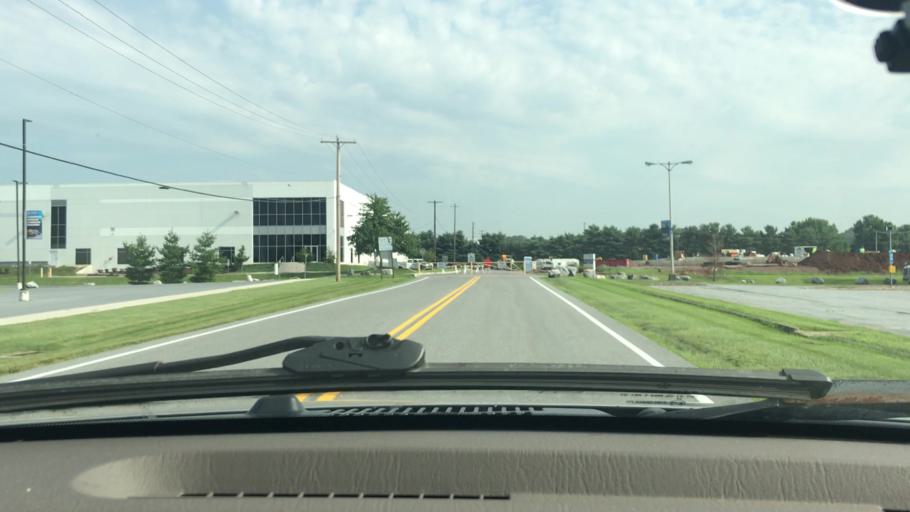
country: US
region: Pennsylvania
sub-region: Dauphin County
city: Middletown
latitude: 40.2067
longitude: -76.7434
